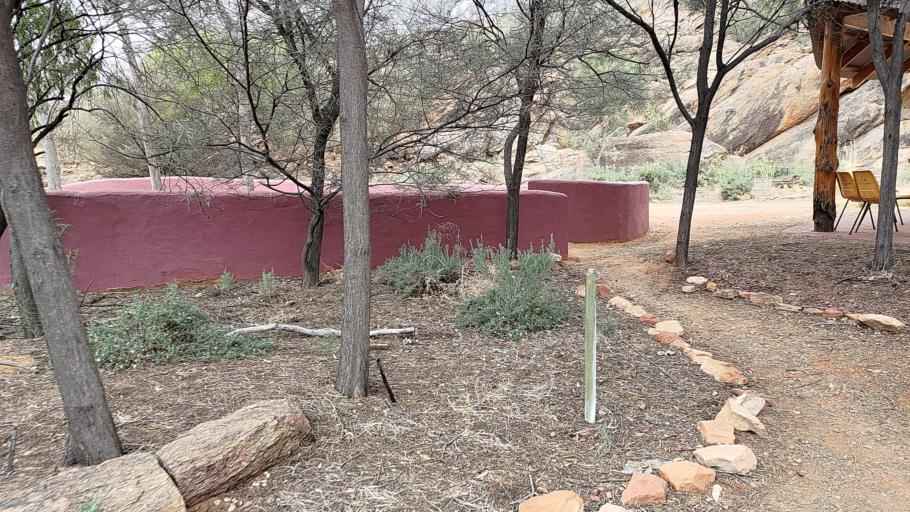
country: AU
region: Northern Territory
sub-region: Alice Springs
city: Alice Springs
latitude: -23.7060
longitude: 133.8837
